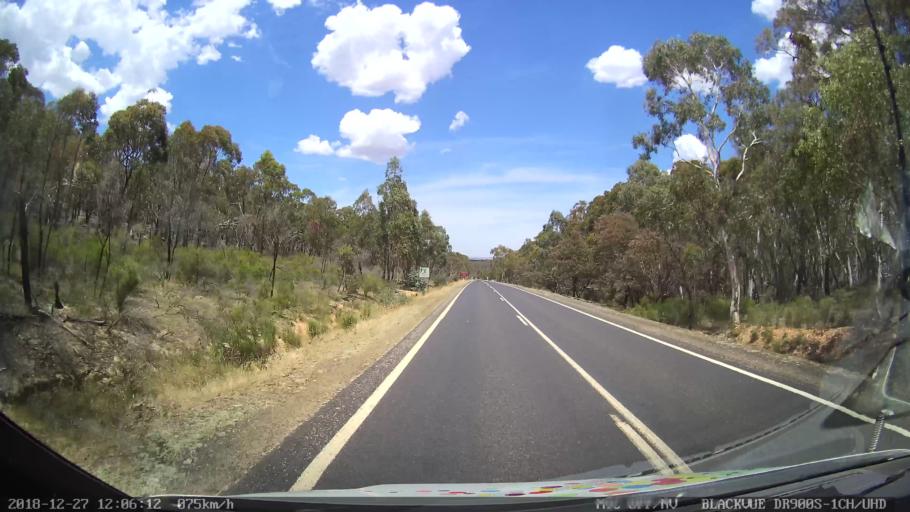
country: AU
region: New South Wales
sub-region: Blayney
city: Blayney
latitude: -33.8068
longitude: 149.3309
